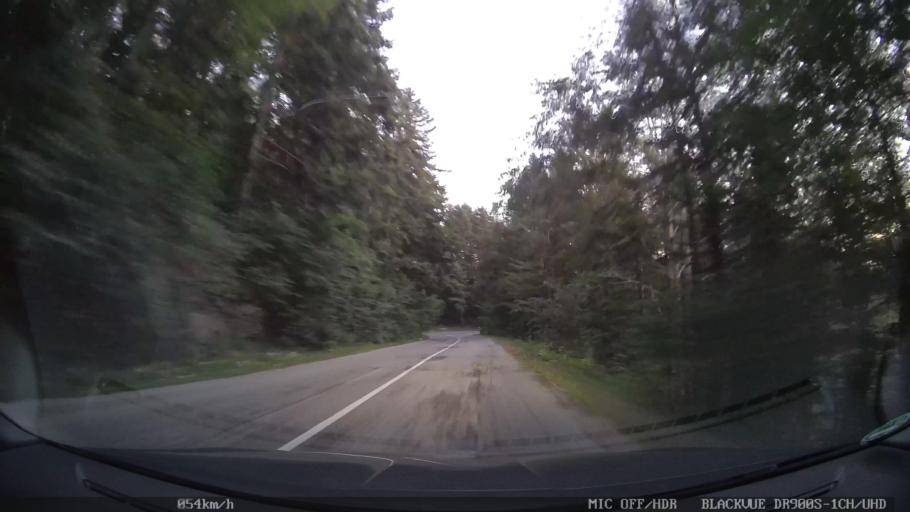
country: HR
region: Primorsko-Goranska
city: Novi Vinodolski
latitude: 45.1968
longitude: 14.8806
